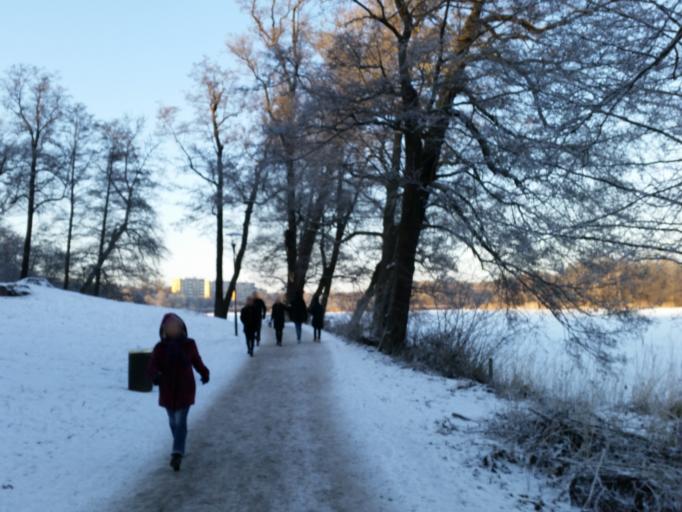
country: SE
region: Stockholm
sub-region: Solna Kommun
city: Rasunda
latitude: 59.3707
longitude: 17.9897
